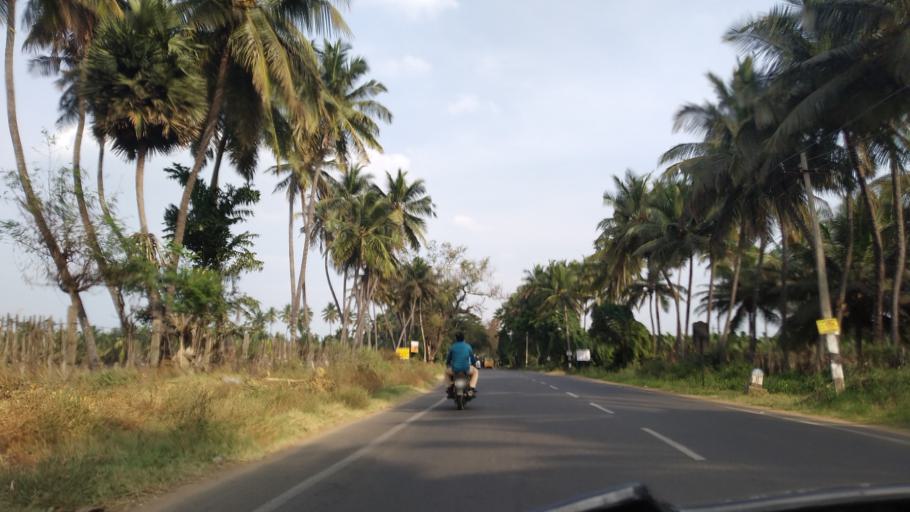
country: IN
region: Tamil Nadu
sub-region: Coimbatore
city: Perur
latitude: 10.9735
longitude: 76.8713
